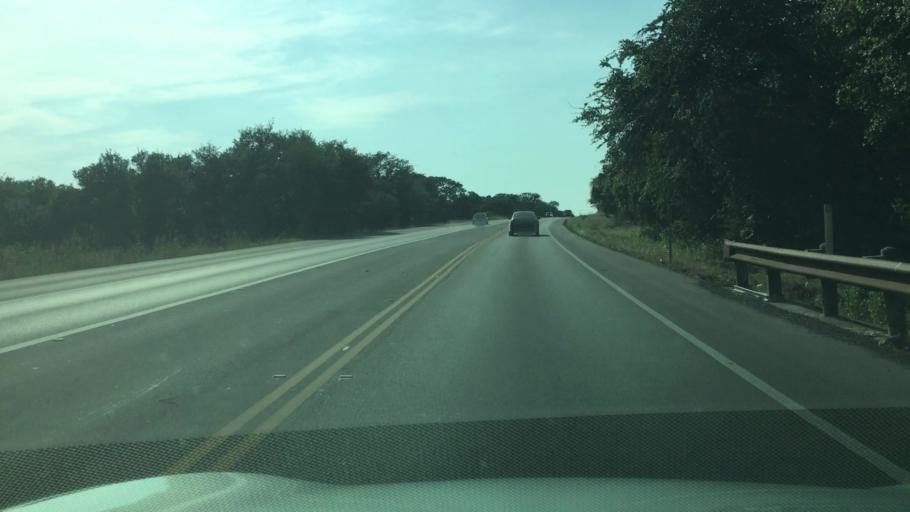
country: US
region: Texas
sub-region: Hays County
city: Wimberley
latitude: 29.9206
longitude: -98.0582
